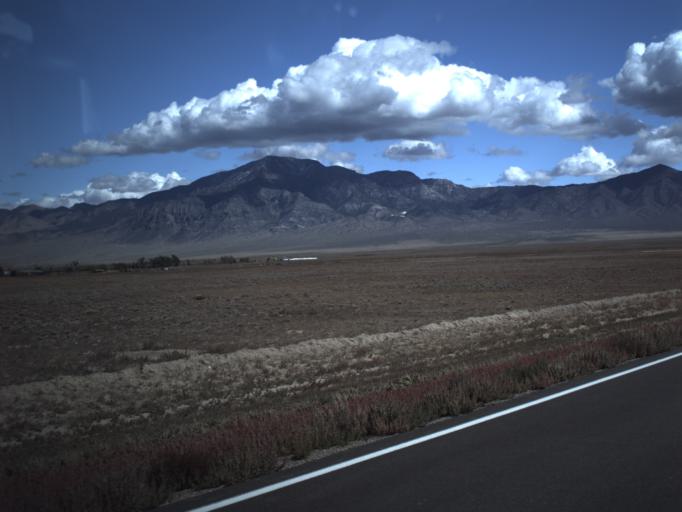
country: US
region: Utah
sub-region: Beaver County
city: Milford
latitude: 38.4806
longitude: -113.4380
